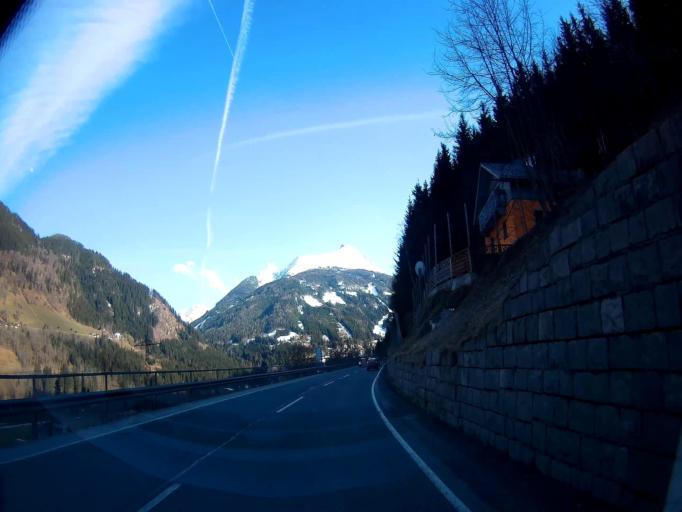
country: AT
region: Salzburg
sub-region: Politischer Bezirk Sankt Johann im Pongau
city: Bad Gastein
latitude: 47.1385
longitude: 13.1241
